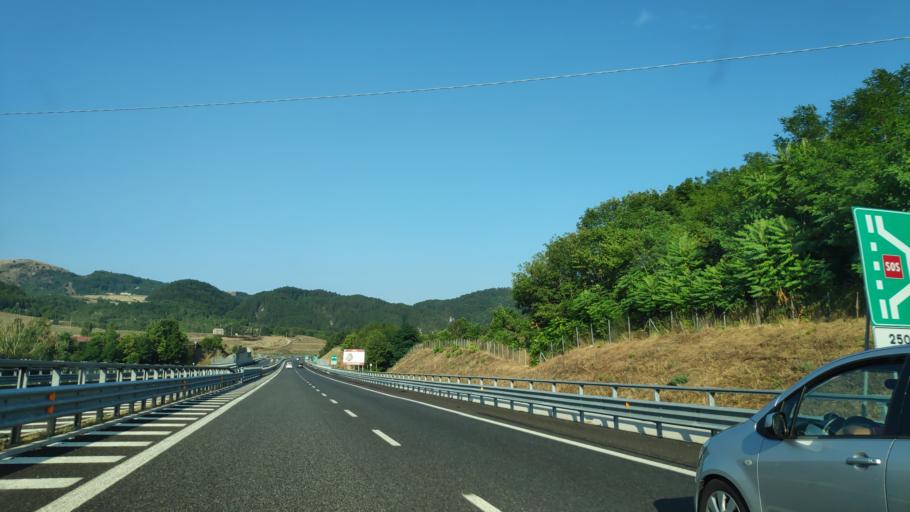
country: IT
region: Calabria
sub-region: Provincia di Cosenza
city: Mormanno
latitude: 39.8780
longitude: 16.0012
